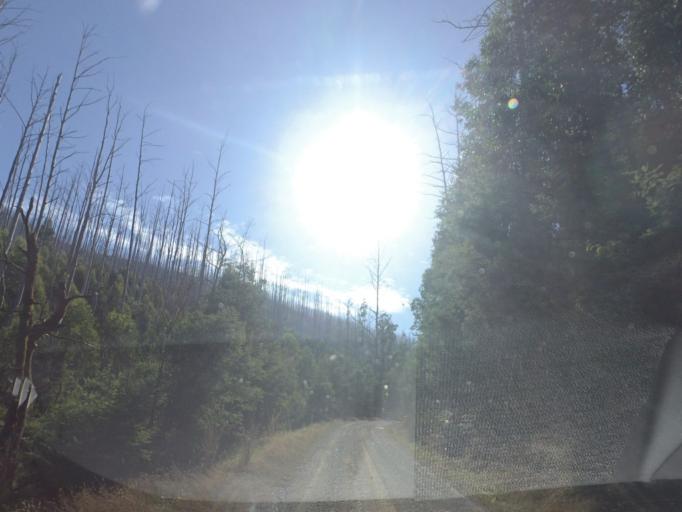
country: AU
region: Victoria
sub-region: Yarra Ranges
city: Millgrove
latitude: -37.4984
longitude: 145.8017
